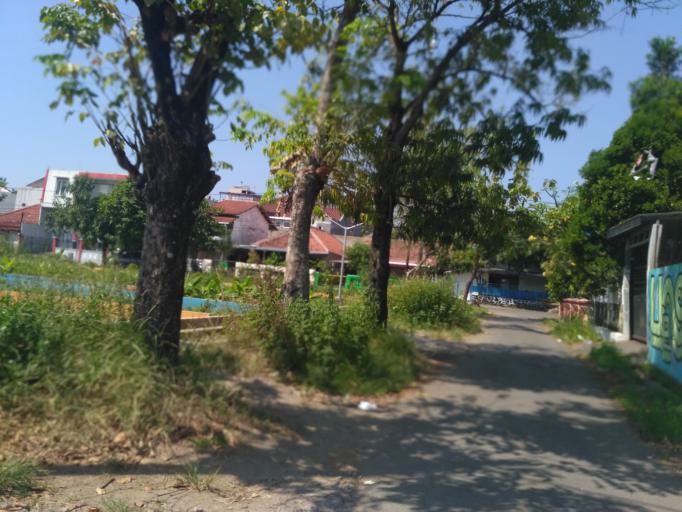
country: ID
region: Central Java
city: Semarang
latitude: -7.0058
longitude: 110.4421
